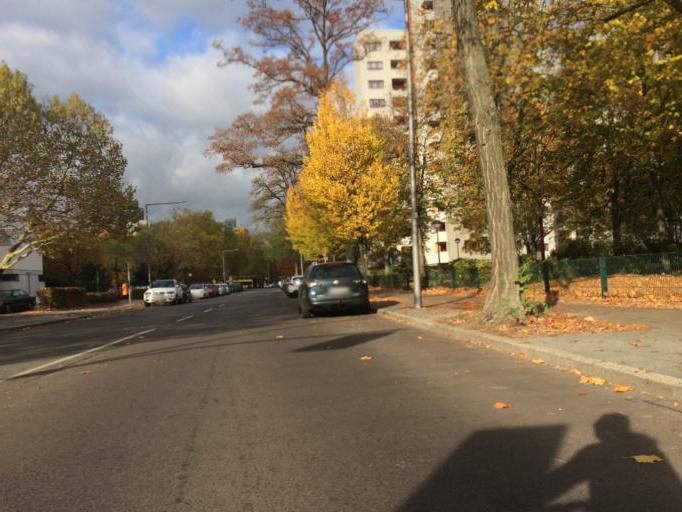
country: DE
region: Berlin
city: Markisches Viertel
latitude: 52.5952
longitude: 13.3608
